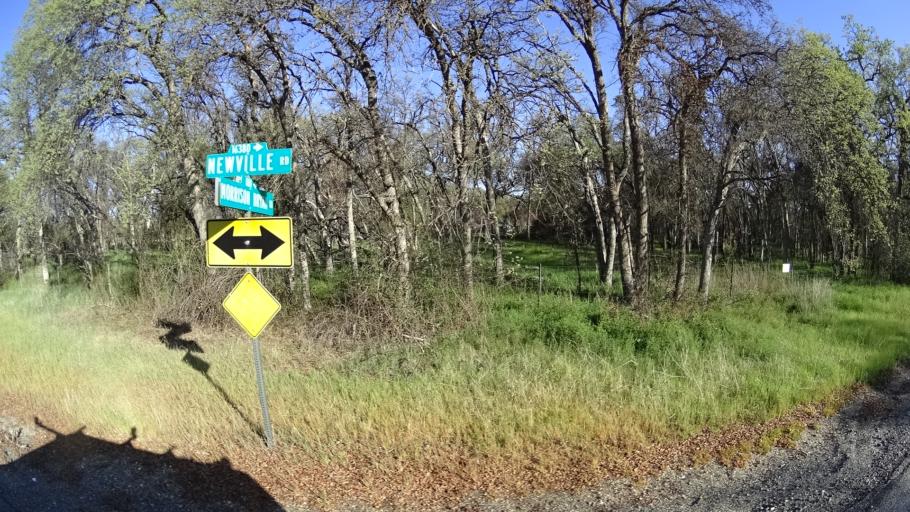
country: US
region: California
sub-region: Tehama County
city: Rancho Tehama Reserve
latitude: 39.7999
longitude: -122.4285
